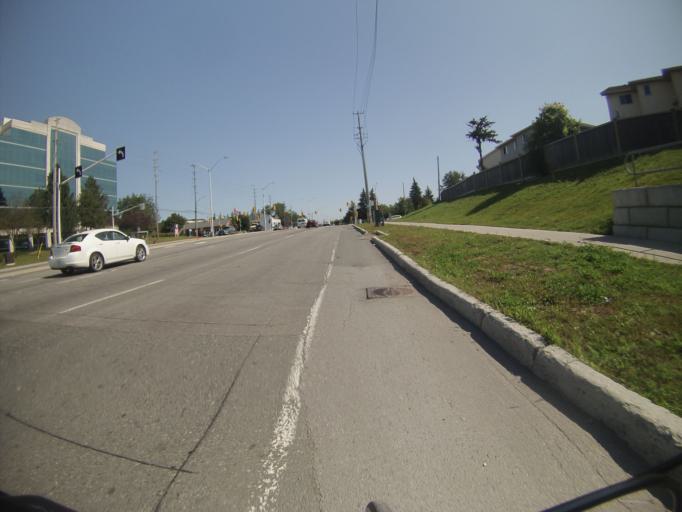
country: CA
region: Ontario
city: Ottawa
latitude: 45.3510
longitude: -75.6524
